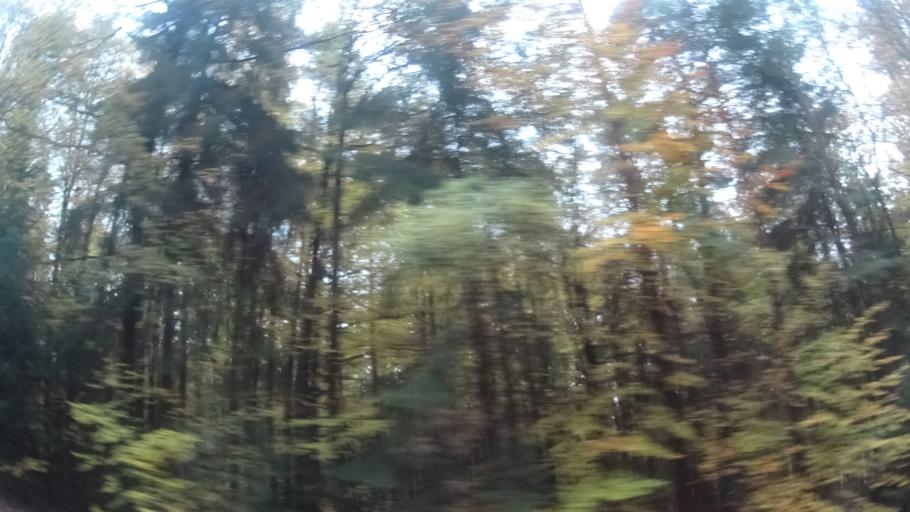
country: DE
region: Bavaria
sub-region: Regierungsbezirk Unterfranken
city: Oberelsbach
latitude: 50.3625
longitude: 10.1018
